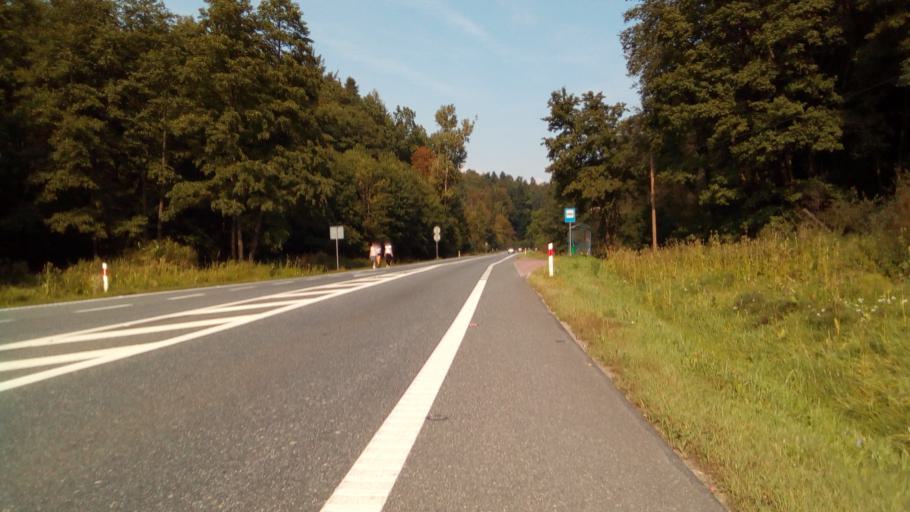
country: PL
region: Subcarpathian Voivodeship
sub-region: Powiat strzyzowski
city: Jawornik
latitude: 49.8262
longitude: 21.8763
